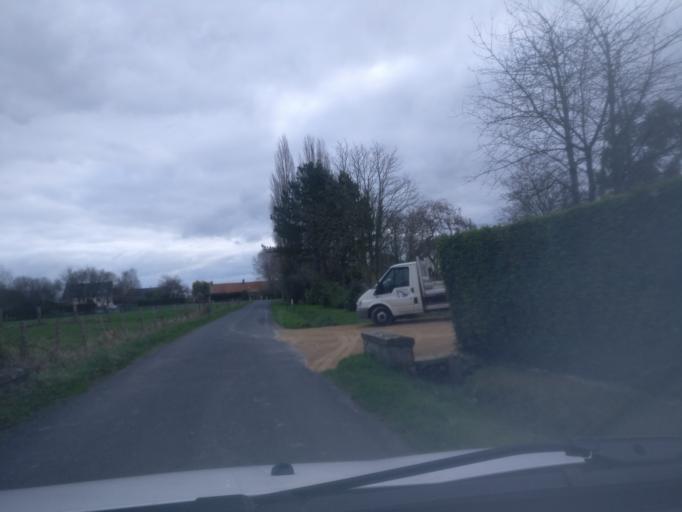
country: FR
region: Lower Normandy
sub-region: Departement de la Manche
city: Marcey-les-Greves
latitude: 48.6674
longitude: -1.4272
